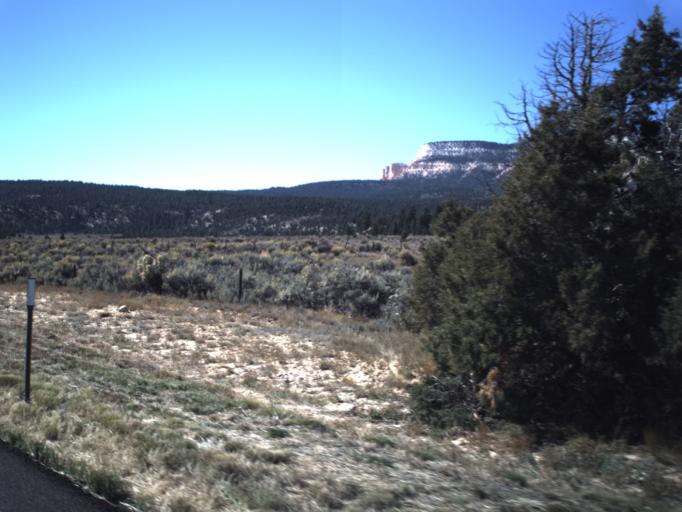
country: US
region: Utah
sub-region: Garfield County
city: Panguitch
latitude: 37.6749
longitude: -111.8256
